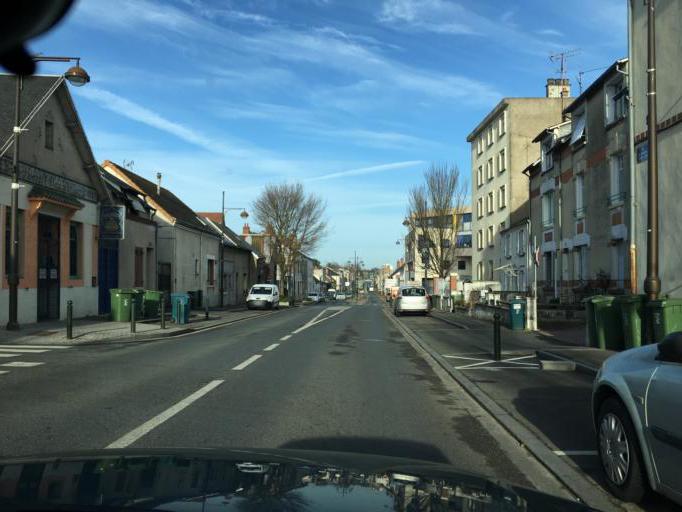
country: FR
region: Centre
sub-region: Departement du Loiret
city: Saint-Jean-de-la-Ruelle
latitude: 47.9089
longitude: 1.8841
